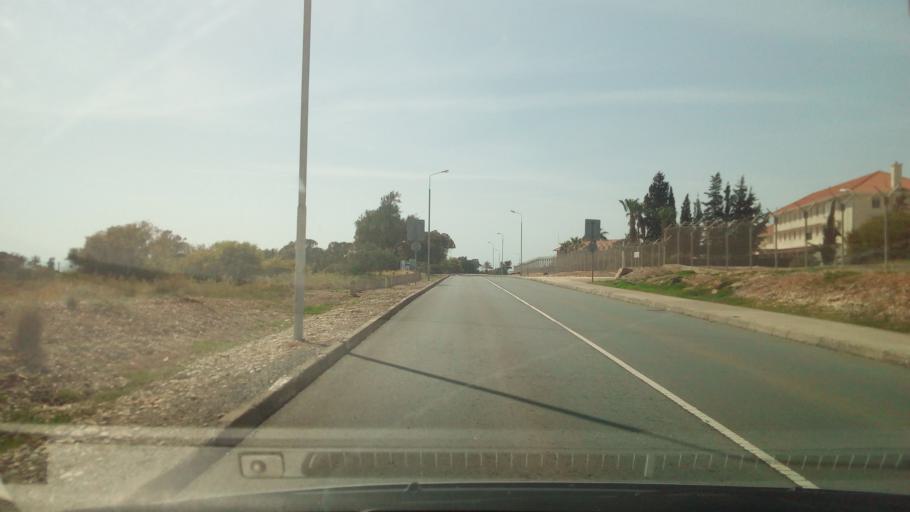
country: CY
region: Larnaka
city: Xylotymbou
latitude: 34.9828
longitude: 33.7320
